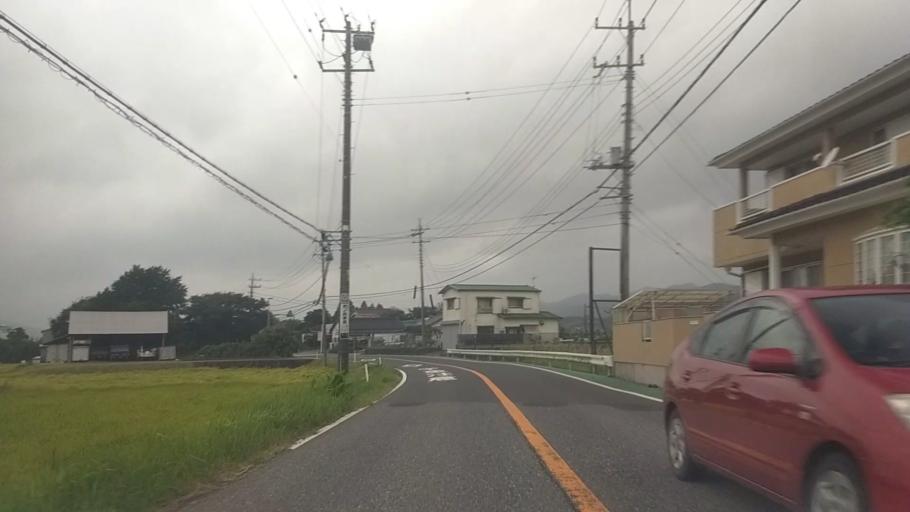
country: JP
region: Chiba
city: Kawaguchi
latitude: 35.1271
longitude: 140.0549
